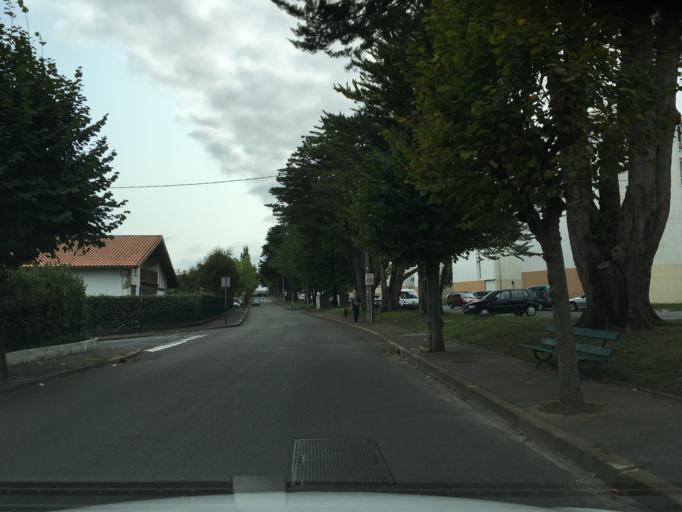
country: FR
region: Aquitaine
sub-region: Departement des Pyrenees-Atlantiques
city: Biarritz
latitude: 43.4752
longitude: -1.5380
